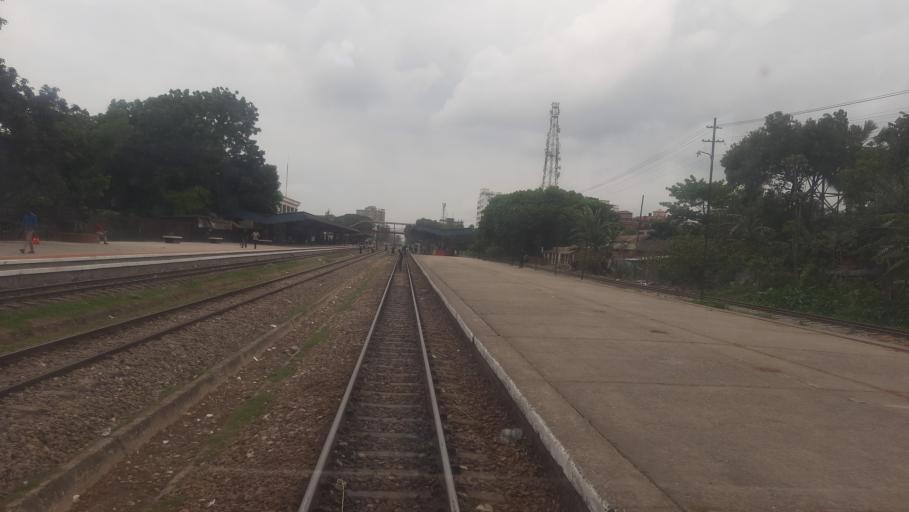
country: BD
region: Chittagong
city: Feni
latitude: 23.0127
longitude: 91.4045
